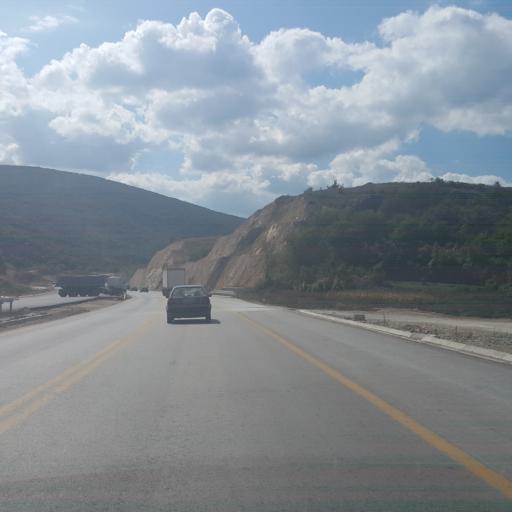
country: RS
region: Central Serbia
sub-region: Pirotski Okrug
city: Bela Palanka
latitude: 43.2287
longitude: 22.4332
